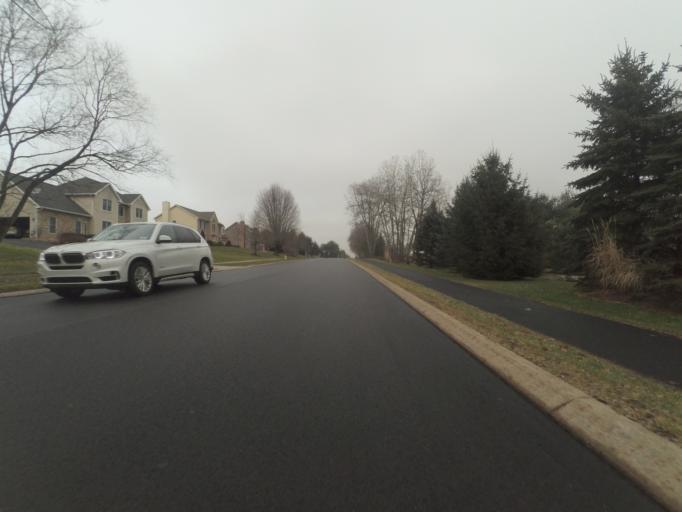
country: US
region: Pennsylvania
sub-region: Centre County
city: Park Forest Village
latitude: 40.7855
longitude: -77.9135
